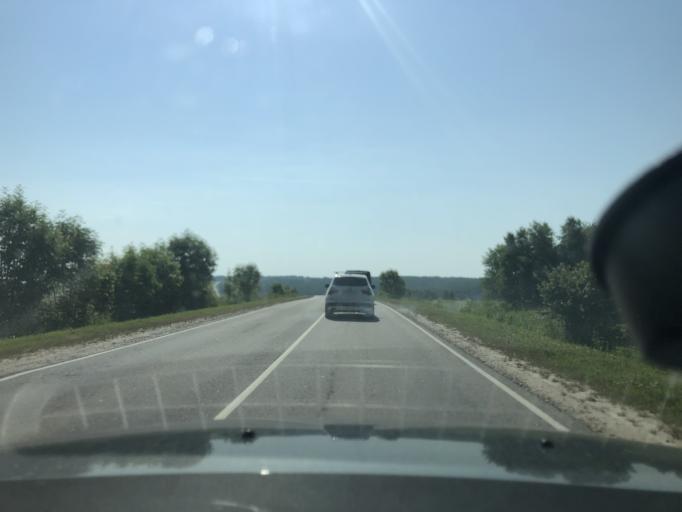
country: RU
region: Tula
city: Dubna
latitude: 54.1335
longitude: 37.0269
